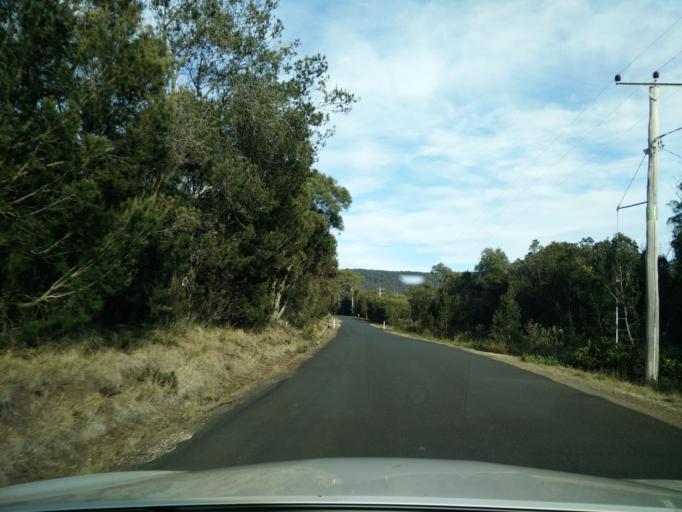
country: AU
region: Tasmania
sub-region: Break O'Day
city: St Helens
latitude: -41.8531
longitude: 148.2627
